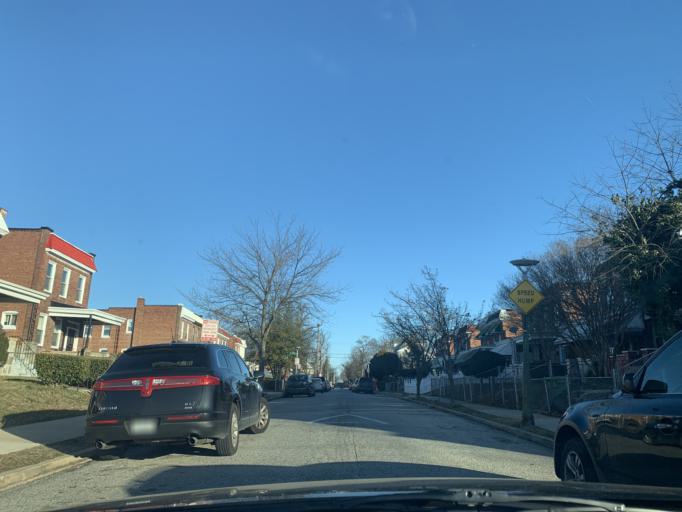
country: US
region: Maryland
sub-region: Baltimore County
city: Lochearn
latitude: 39.3319
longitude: -76.6870
